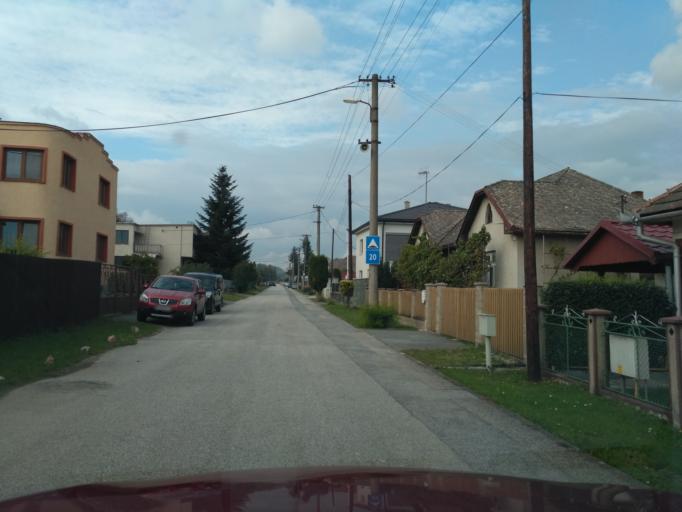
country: SK
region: Kosicky
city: Kosice
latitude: 48.6379
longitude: 21.1691
